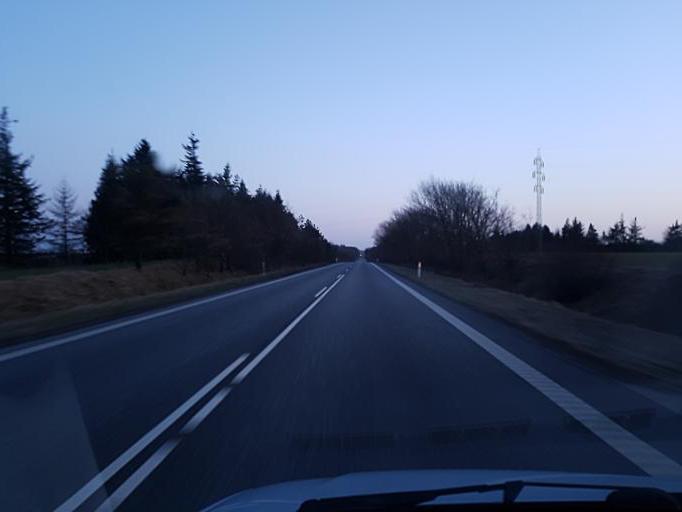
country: DK
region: Central Jutland
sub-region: Holstebro Kommune
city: Holstebro
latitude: 56.2373
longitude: 8.6068
